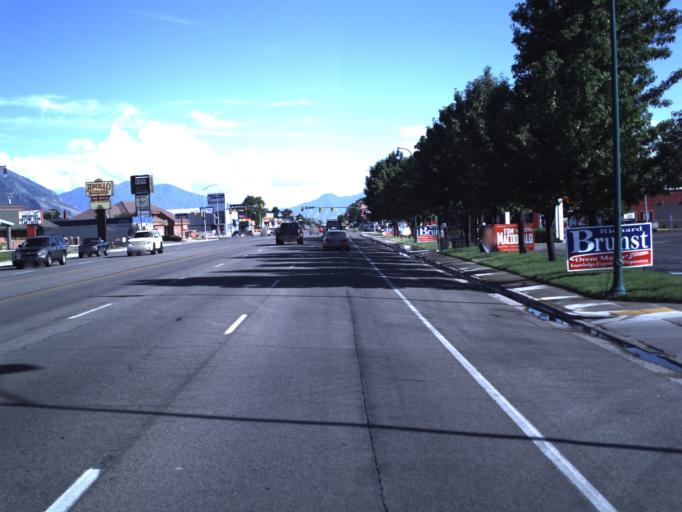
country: US
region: Utah
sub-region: Utah County
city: Orem
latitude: 40.3063
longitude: -111.6992
